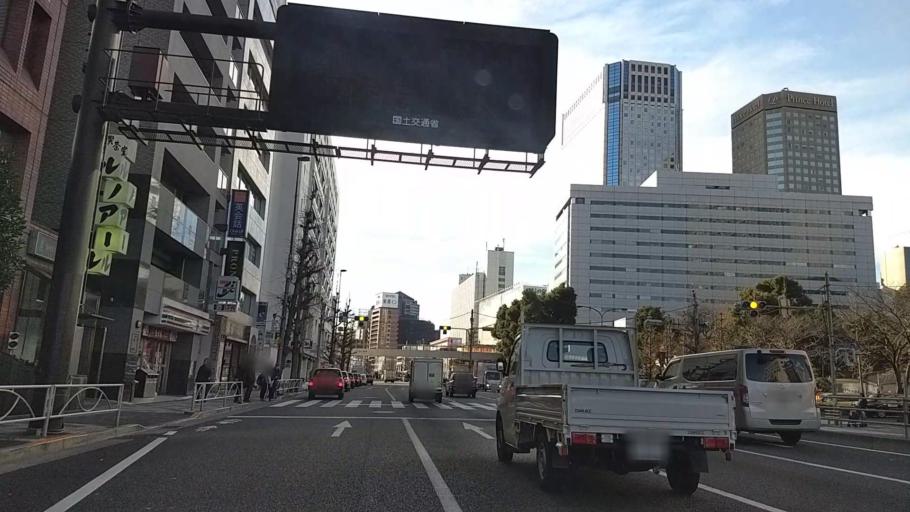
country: JP
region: Tokyo
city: Tokyo
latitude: 35.6308
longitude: 139.7376
